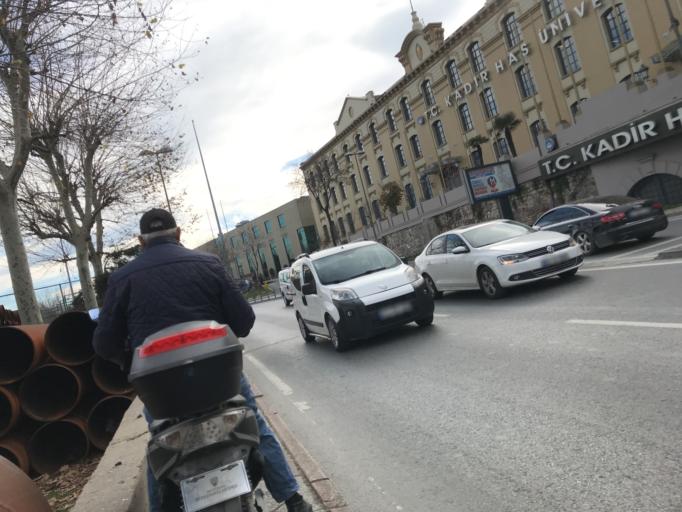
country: TR
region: Istanbul
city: Istanbul
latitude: 41.0252
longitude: 28.9594
